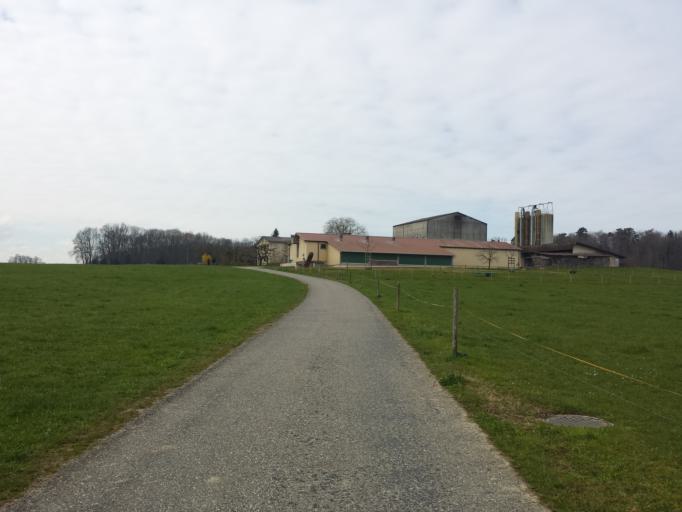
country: CH
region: Thurgau
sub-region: Arbon District
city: Salmsach
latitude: 47.5710
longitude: 9.3587
